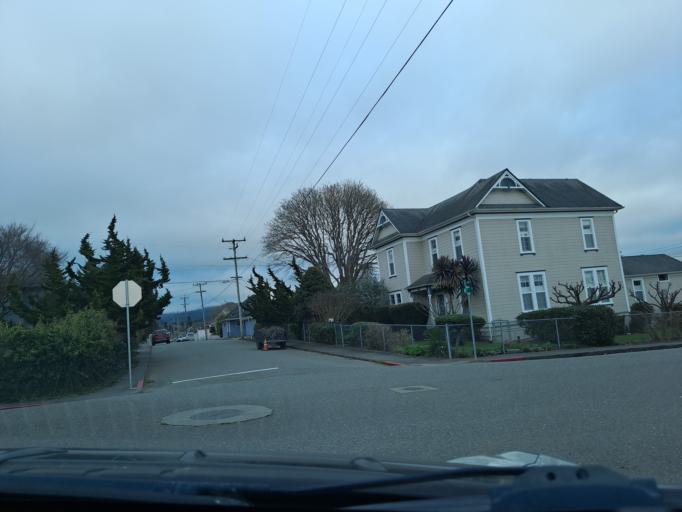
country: US
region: California
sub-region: Humboldt County
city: Fortuna
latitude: 40.5994
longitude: -124.1616
